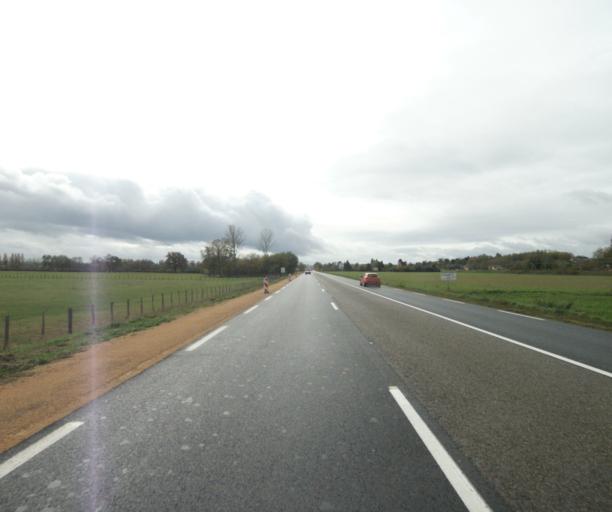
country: FR
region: Rhone-Alpes
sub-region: Departement de l'Ain
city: Pont-de-Vaux
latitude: 46.4572
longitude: 4.8900
